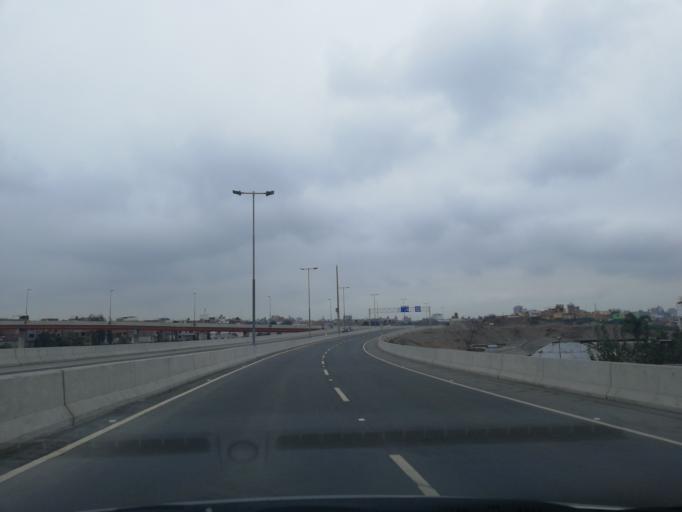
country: PE
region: Lima
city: Lima
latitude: -12.0406
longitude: -77.0143
